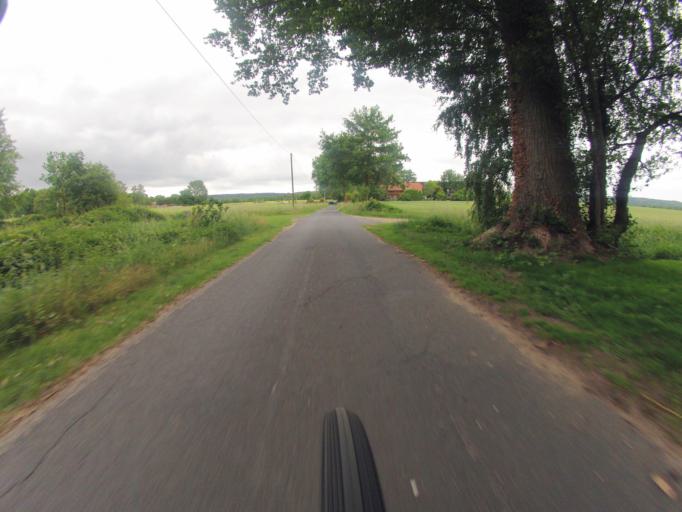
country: DE
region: North Rhine-Westphalia
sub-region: Regierungsbezirk Munster
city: Tecklenburg
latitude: 52.2538
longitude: 7.7727
